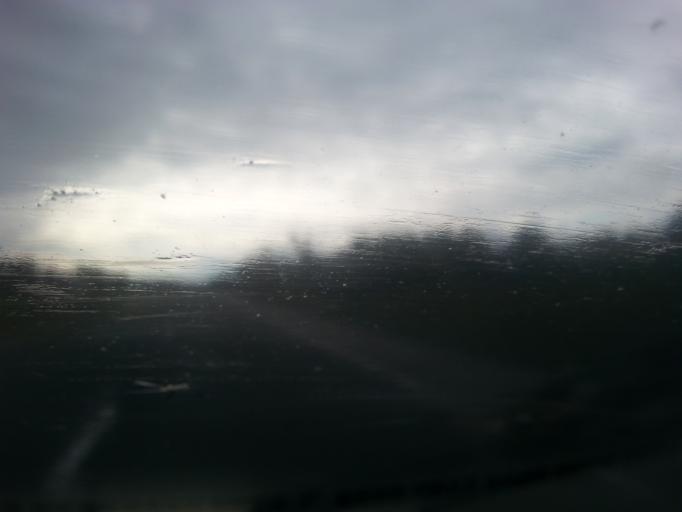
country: CA
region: Ontario
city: Quinte West
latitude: 44.0411
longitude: -77.8504
